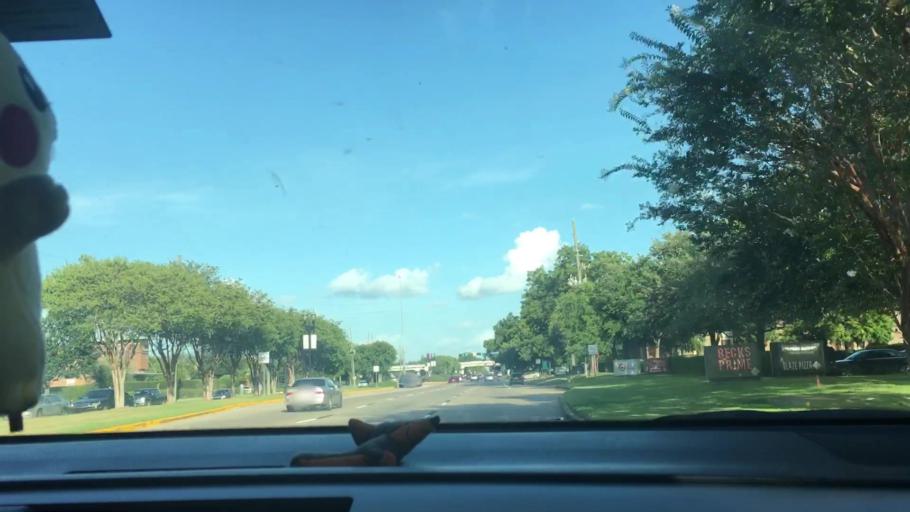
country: US
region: Texas
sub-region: Fort Bend County
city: Sugar Land
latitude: 29.6000
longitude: -95.6273
